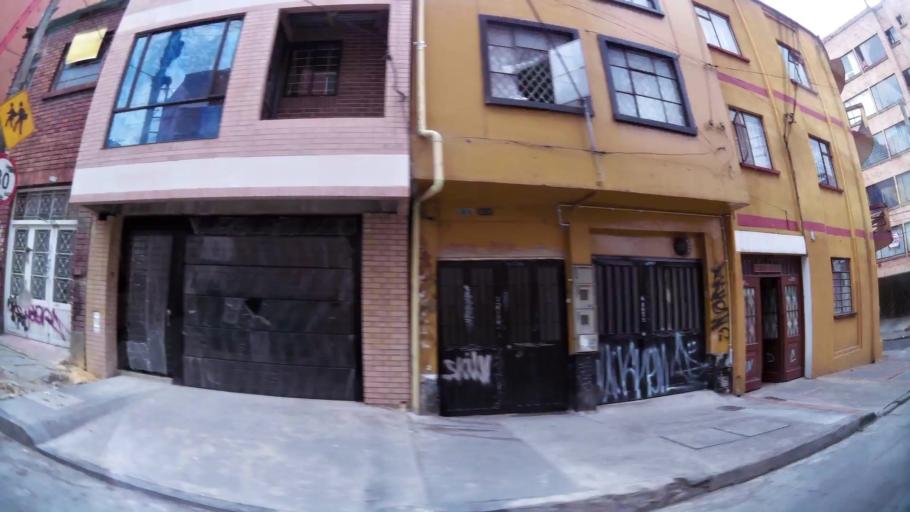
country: CO
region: Bogota D.C.
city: Bogota
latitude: 4.6350
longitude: -74.0648
